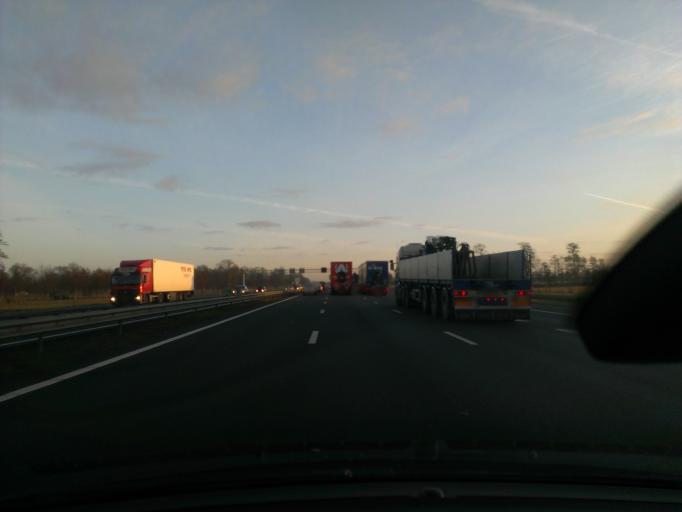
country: NL
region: Overijssel
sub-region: Gemeente Staphorst
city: Staphorst
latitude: 52.5904
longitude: 6.1972
